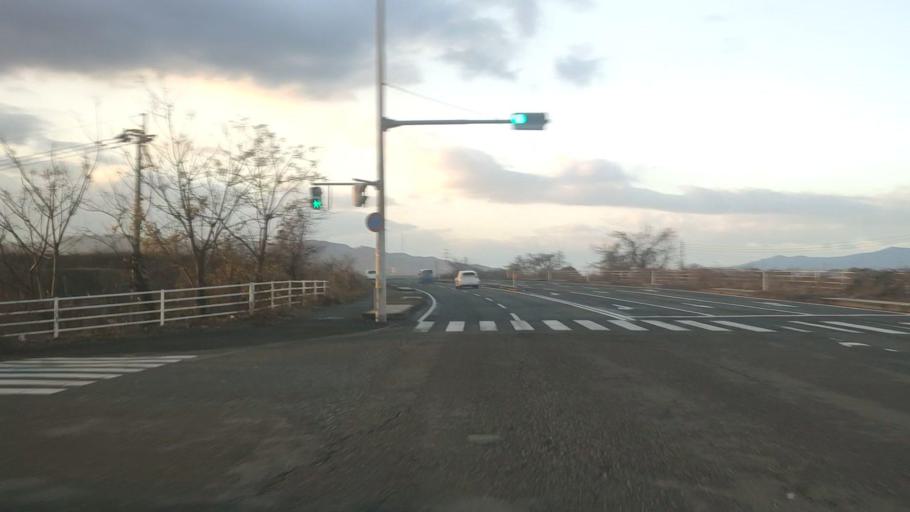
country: JP
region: Kumamoto
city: Kumamoto
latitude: 32.7424
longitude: 130.7049
